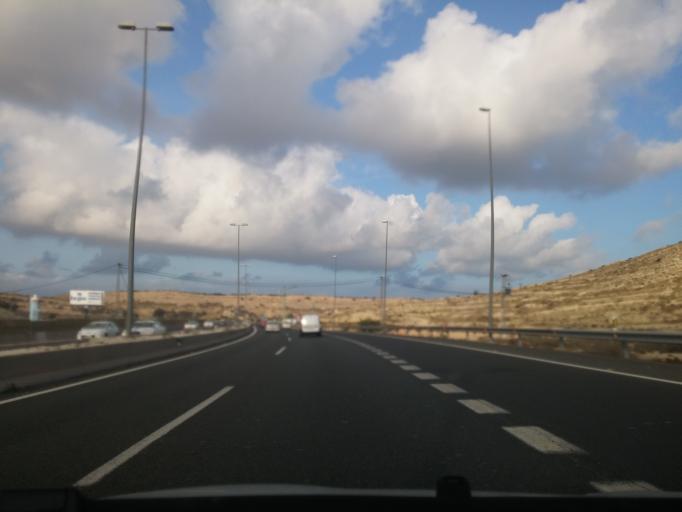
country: ES
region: Valencia
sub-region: Provincia de Alicante
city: Alicante
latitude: 38.3840
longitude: -0.4843
